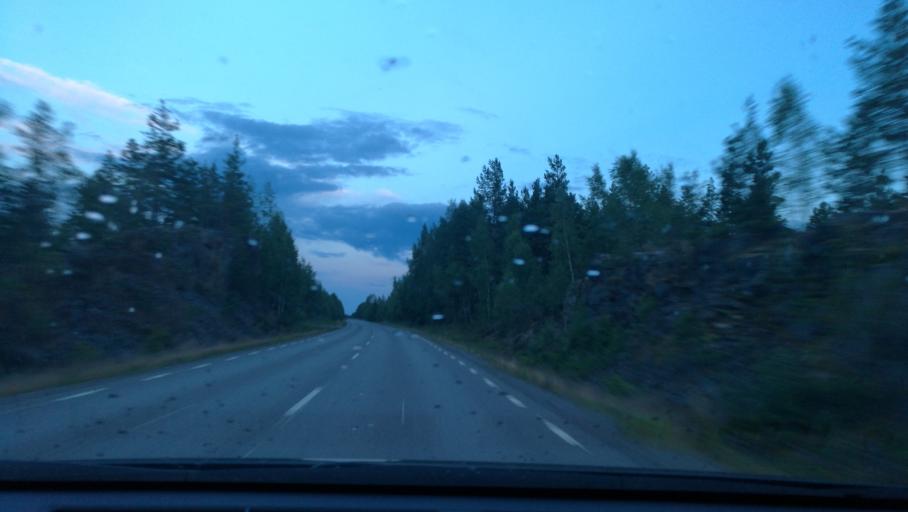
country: SE
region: OEstergoetland
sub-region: Norrkopings Kommun
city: Svartinge
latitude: 58.8019
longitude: 15.9439
